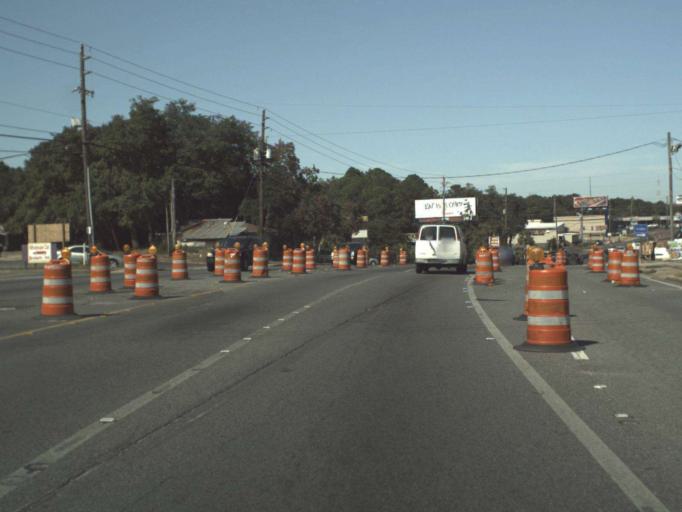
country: US
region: Florida
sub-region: Okaloosa County
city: Wright
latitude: 30.4302
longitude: -86.6394
